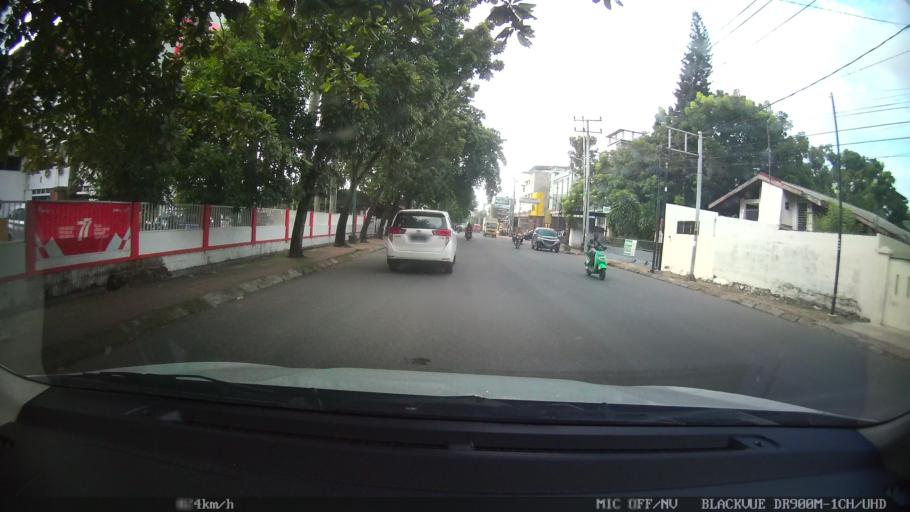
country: ID
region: North Sumatra
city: Medan
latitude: 3.5974
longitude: 98.6781
